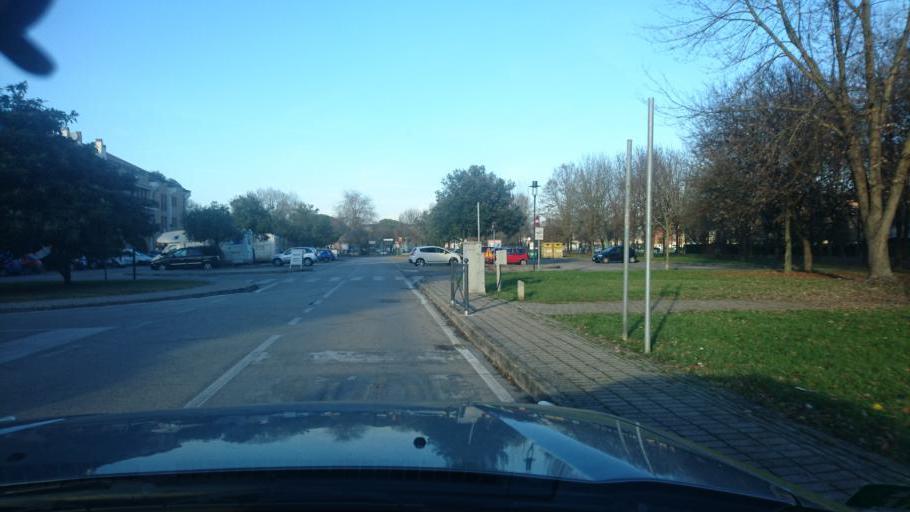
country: IT
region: Veneto
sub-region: Provincia di Padova
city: San Vito
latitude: 45.4279
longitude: 11.9620
